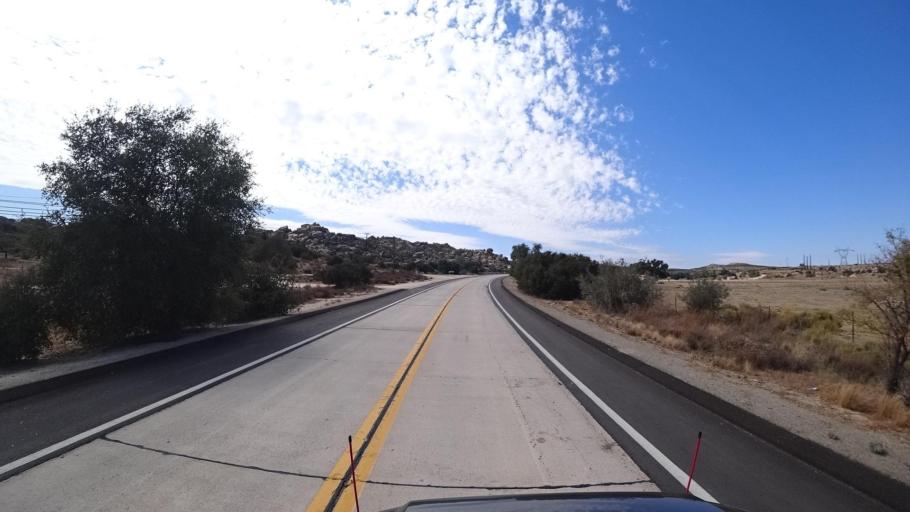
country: MX
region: Baja California
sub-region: Tecate
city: Cereso del Hongo
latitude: 32.6613
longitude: -116.2561
